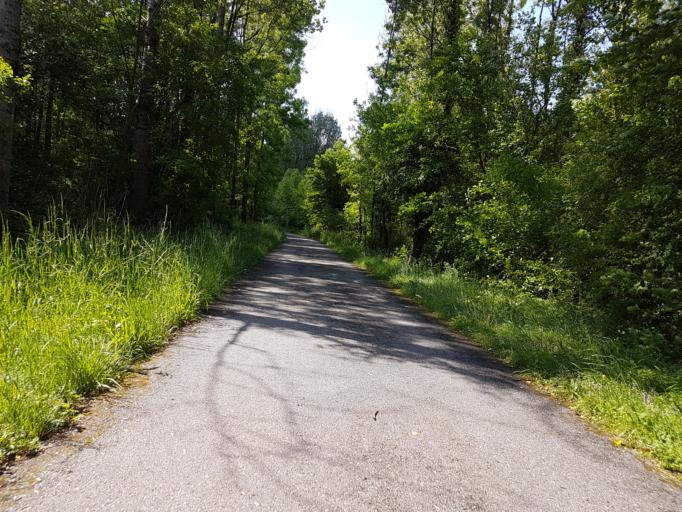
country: FR
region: Rhone-Alpes
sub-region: Departement de l'Ain
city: Culoz
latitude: 45.8121
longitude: 5.7912
